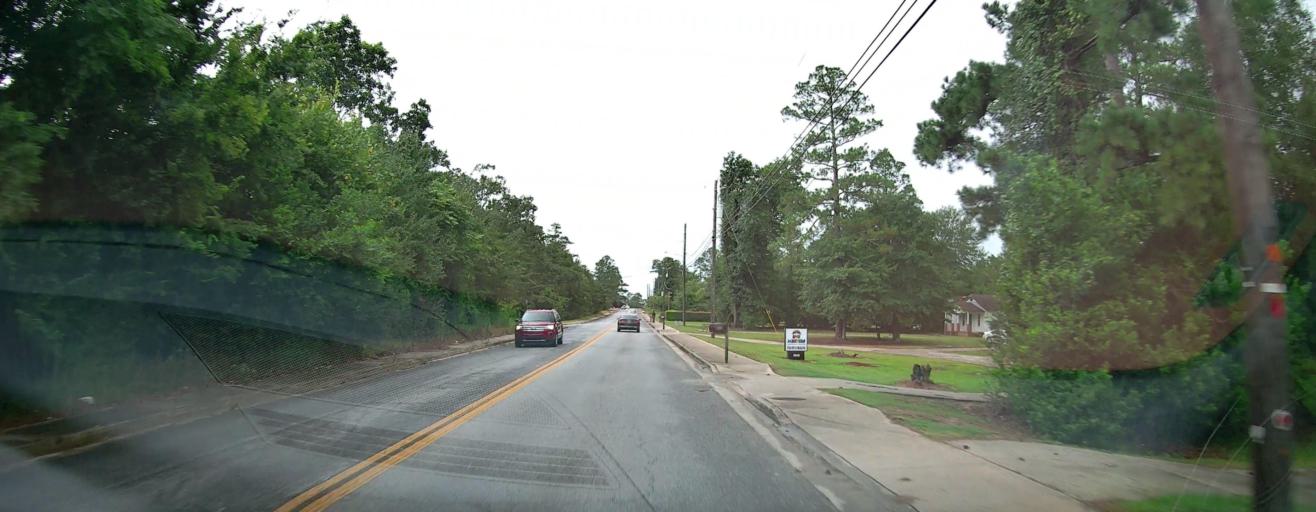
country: US
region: Georgia
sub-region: Bibb County
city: Macon
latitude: 32.8094
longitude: -83.7004
